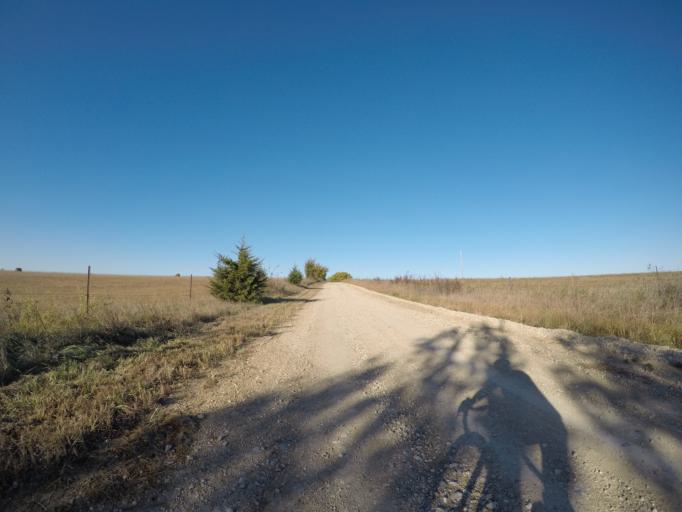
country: US
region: Kansas
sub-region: Wabaunsee County
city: Alma
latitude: 38.9275
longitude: -96.4645
